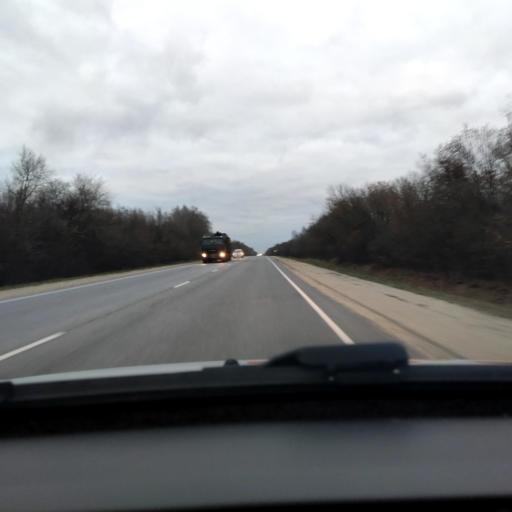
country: RU
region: Lipetsk
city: Khlevnoye
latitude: 52.3353
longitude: 39.1799
